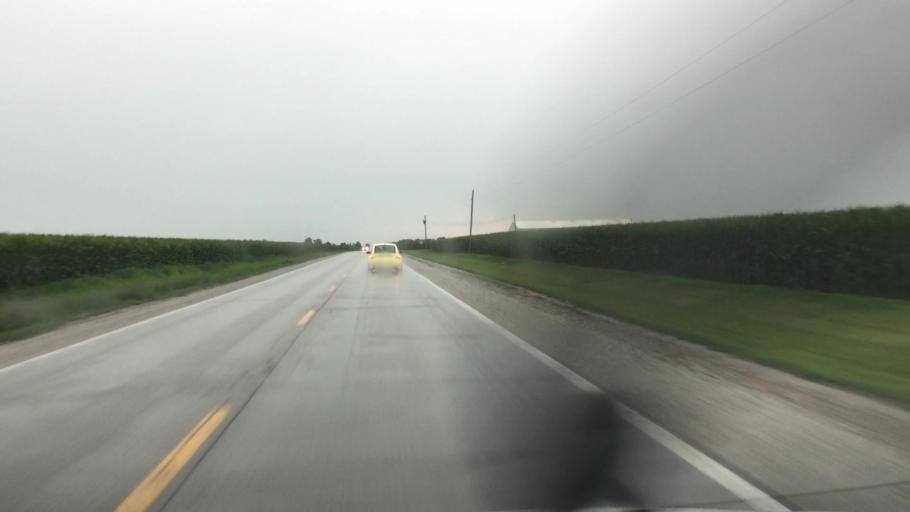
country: US
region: Illinois
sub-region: Hancock County
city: Carthage
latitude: 40.4470
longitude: -91.1398
